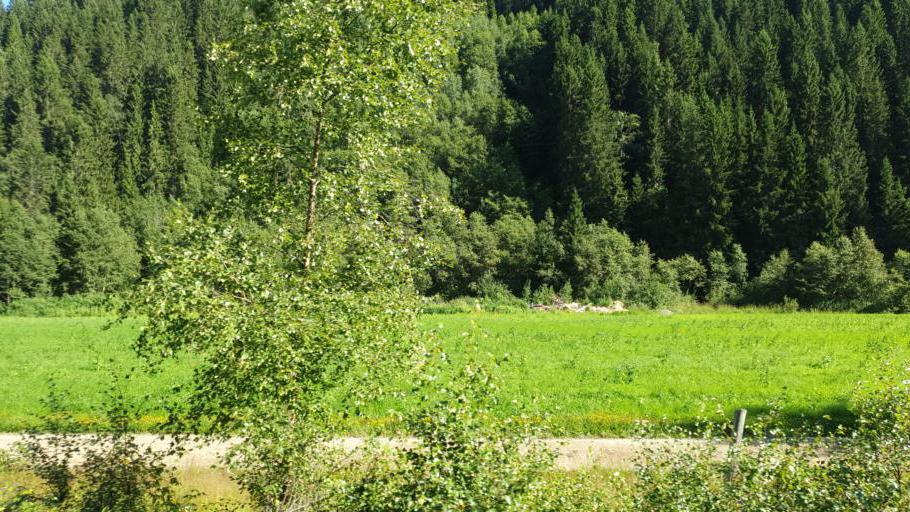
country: NO
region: Sor-Trondelag
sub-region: Orkdal
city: Orkanger
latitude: 63.1929
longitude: 9.7837
